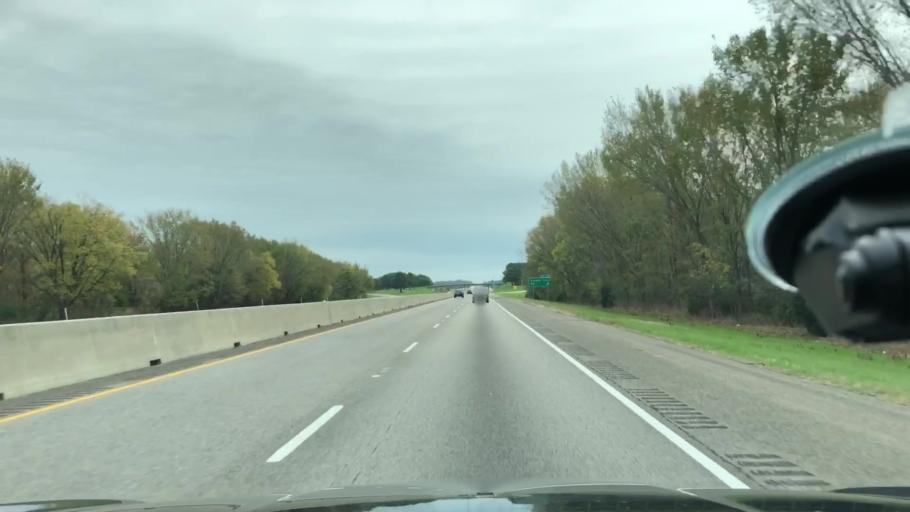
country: US
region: Texas
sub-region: Franklin County
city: Mount Vernon
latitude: 33.1665
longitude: -95.3148
